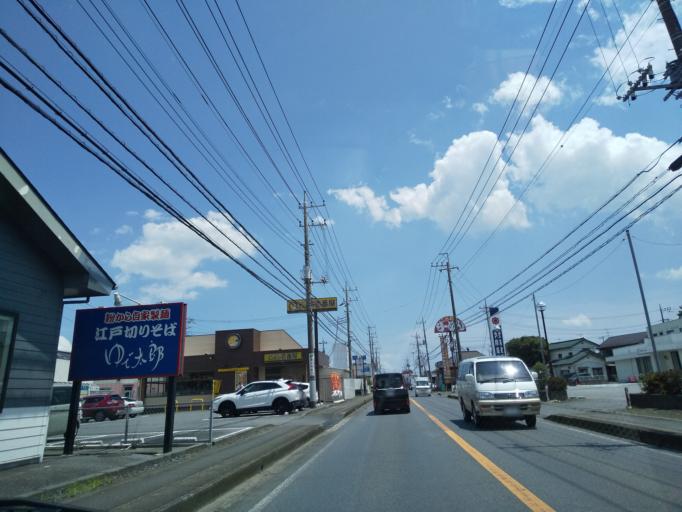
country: JP
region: Ibaraki
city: Ishioka
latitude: 36.1841
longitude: 140.3036
